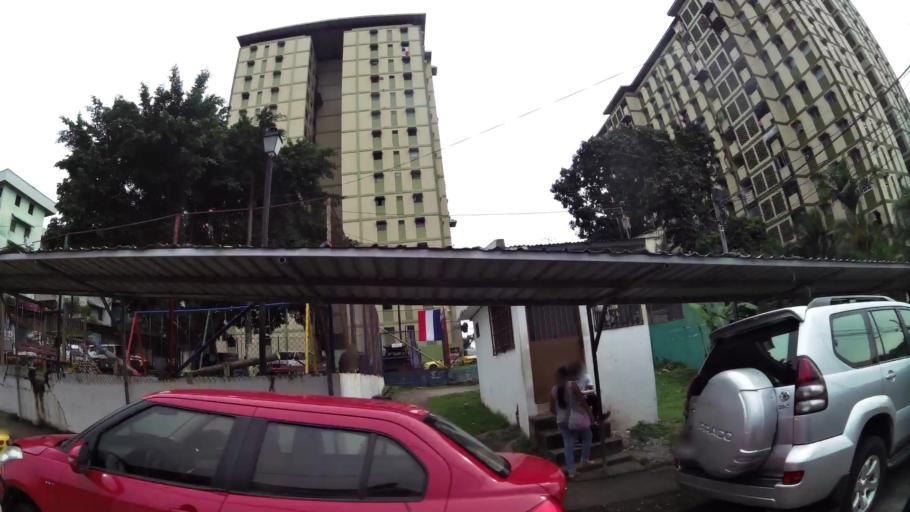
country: PA
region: Panama
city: Panama
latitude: 9.0238
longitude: -79.5244
